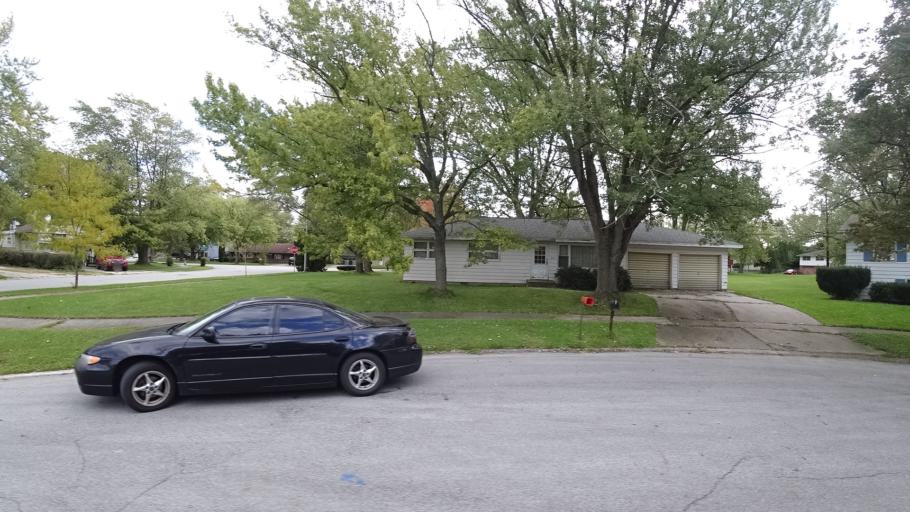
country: US
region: Indiana
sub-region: LaPorte County
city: Michigan City
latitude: 41.6718
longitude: -86.9014
